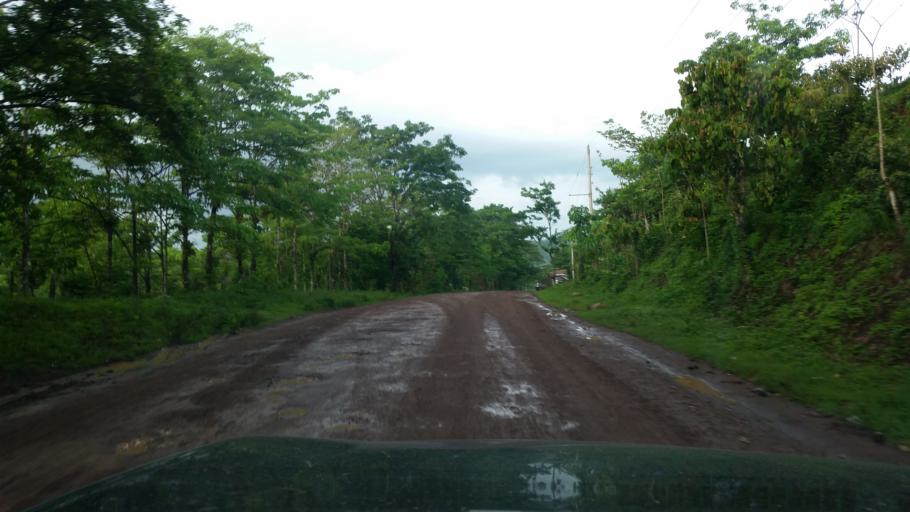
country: NI
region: Atlantico Norte (RAAN)
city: Siuna
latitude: 13.3686
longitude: -84.8723
